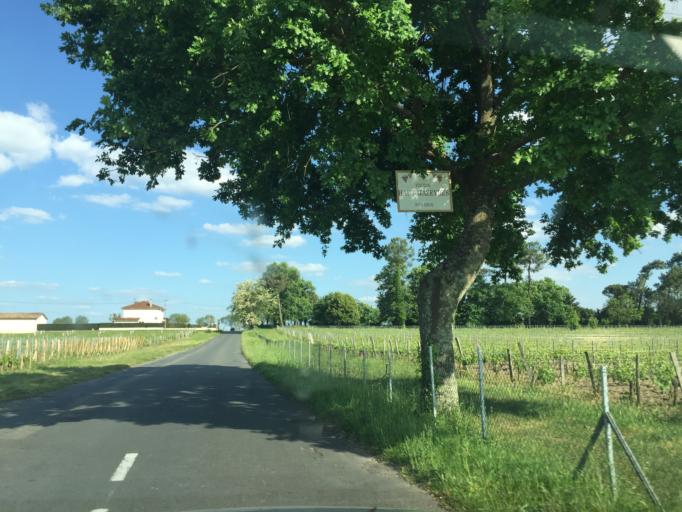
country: FR
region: Aquitaine
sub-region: Departement de la Gironde
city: Libourne
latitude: 44.9350
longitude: -0.2313
